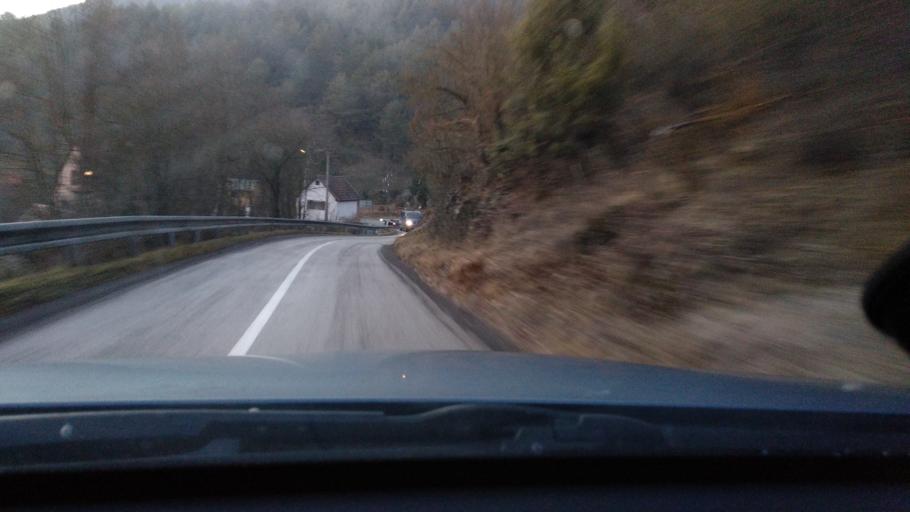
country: SK
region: Nitriansky
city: Banovce nad Bebravou
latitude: 48.8564
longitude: 18.3013
